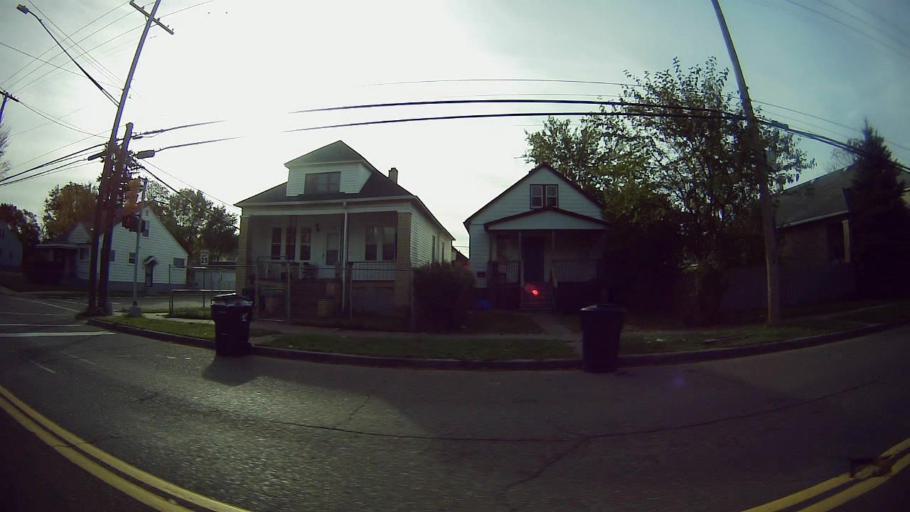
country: US
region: Michigan
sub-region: Wayne County
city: Hamtramck
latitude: 42.4117
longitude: -83.0526
